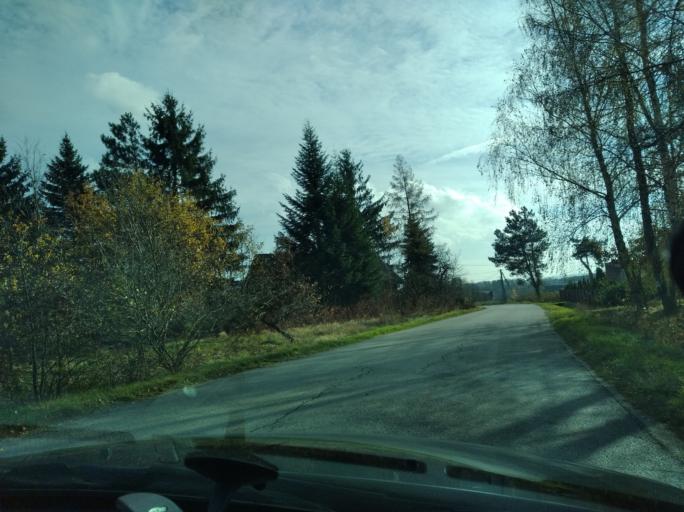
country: PL
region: Subcarpathian Voivodeship
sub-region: Powiat ropczycko-sedziszowski
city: Sedziszow Malopolski
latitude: 50.1182
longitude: 21.7296
